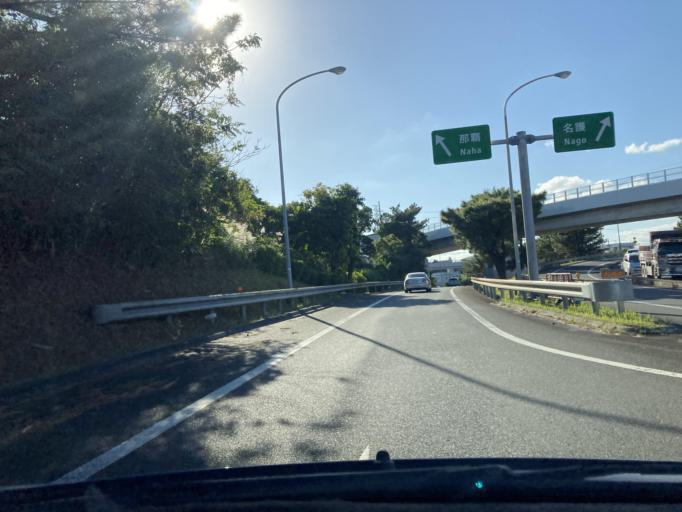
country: JP
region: Okinawa
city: Okinawa
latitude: 26.3738
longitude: 127.8195
